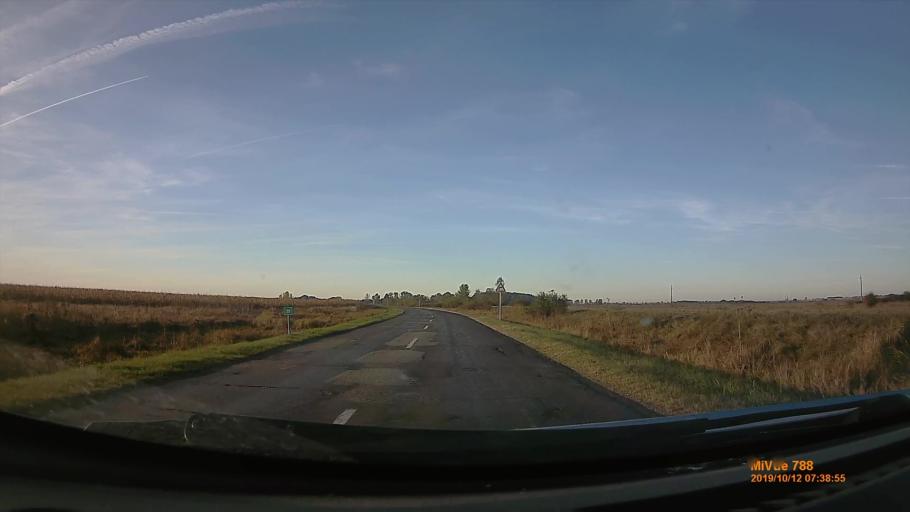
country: HU
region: Hajdu-Bihar
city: Pocsaj
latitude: 47.2195
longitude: 21.8063
